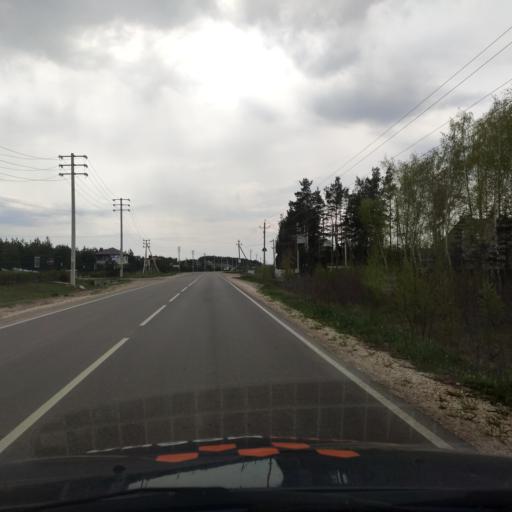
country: RU
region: Voronezj
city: Podgornoye
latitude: 51.8587
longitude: 39.1635
